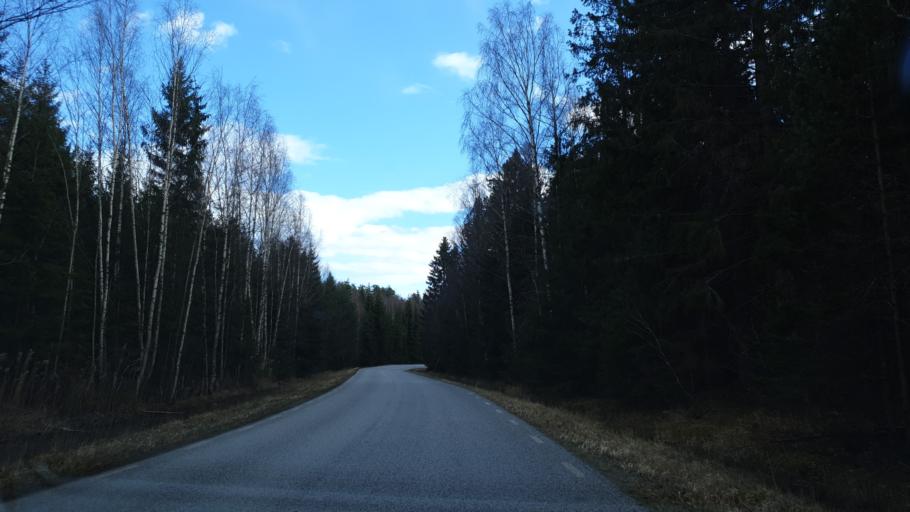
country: SE
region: Stockholm
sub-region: Varmdo Kommun
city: Hemmesta
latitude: 59.2382
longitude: 18.4775
